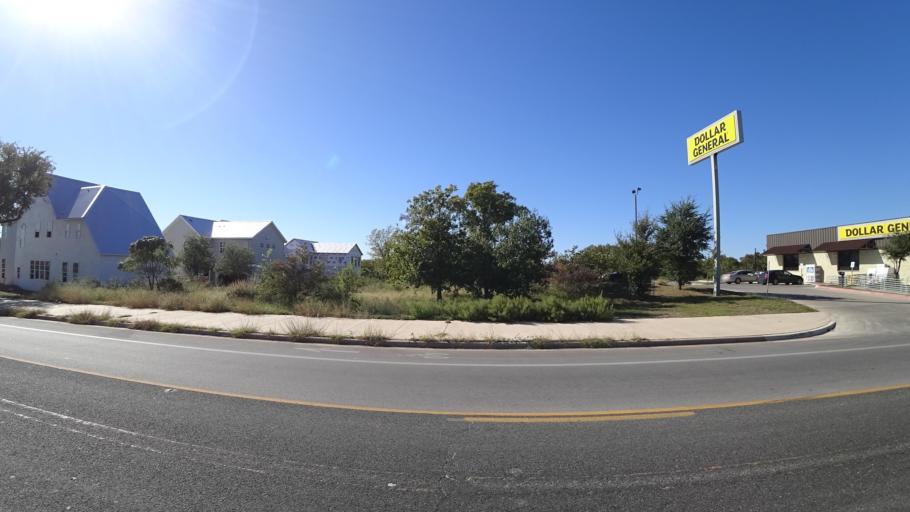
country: US
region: Texas
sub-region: Travis County
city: Austin
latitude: 30.2928
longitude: -97.6782
